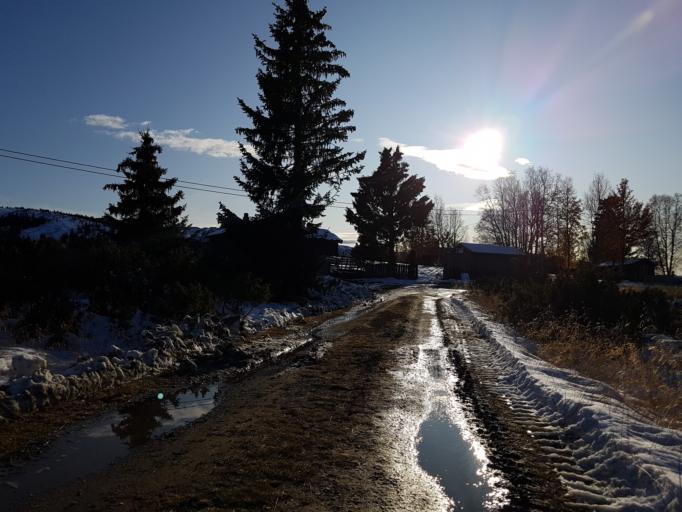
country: NO
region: Oppland
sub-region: Sel
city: Otta
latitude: 61.8119
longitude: 9.6803
